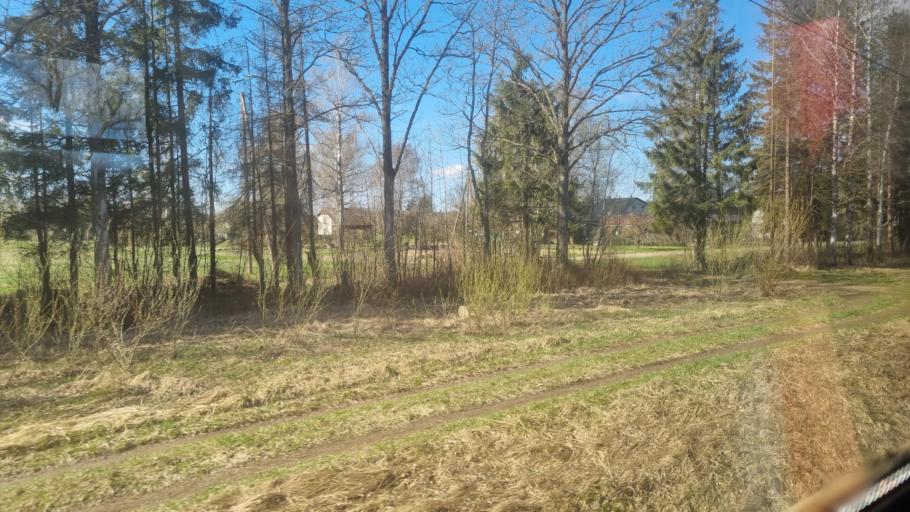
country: LV
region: Lielvarde
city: Lielvarde
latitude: 56.7205
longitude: 24.8205
